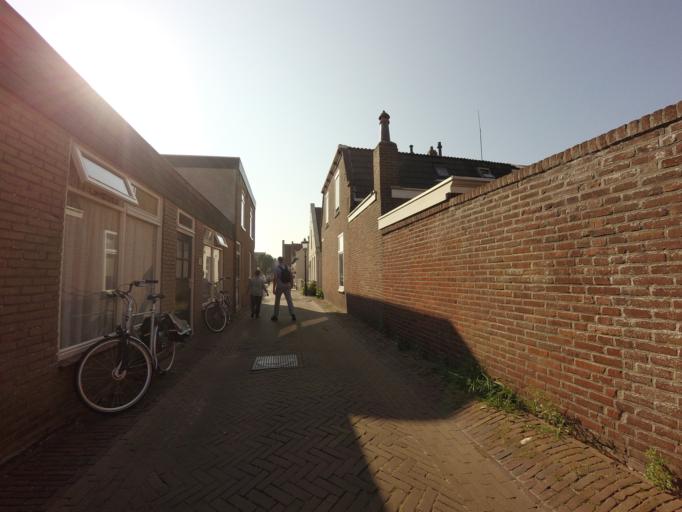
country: NL
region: Friesland
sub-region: Gemeente Terschelling
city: West-Terschelling
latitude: 53.3594
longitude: 5.2138
